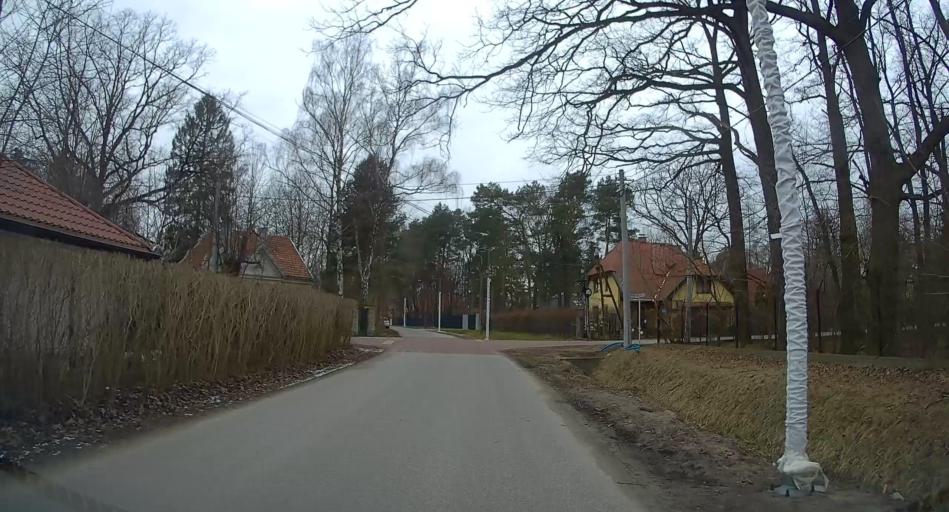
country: PL
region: Masovian Voivodeship
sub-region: Powiat piaseczynski
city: Piaseczno
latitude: 52.0631
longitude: 20.9985
